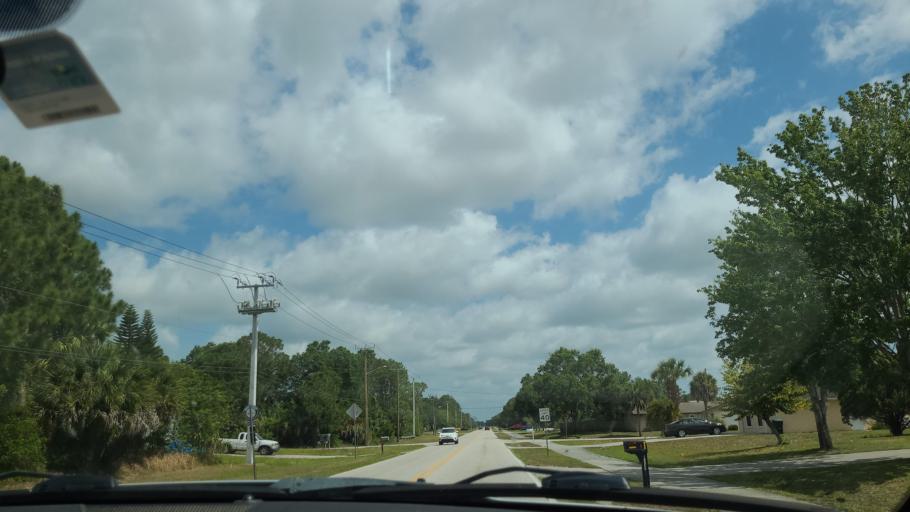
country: US
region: Florida
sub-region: Brevard County
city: June Park
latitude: 28.0049
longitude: -80.6969
